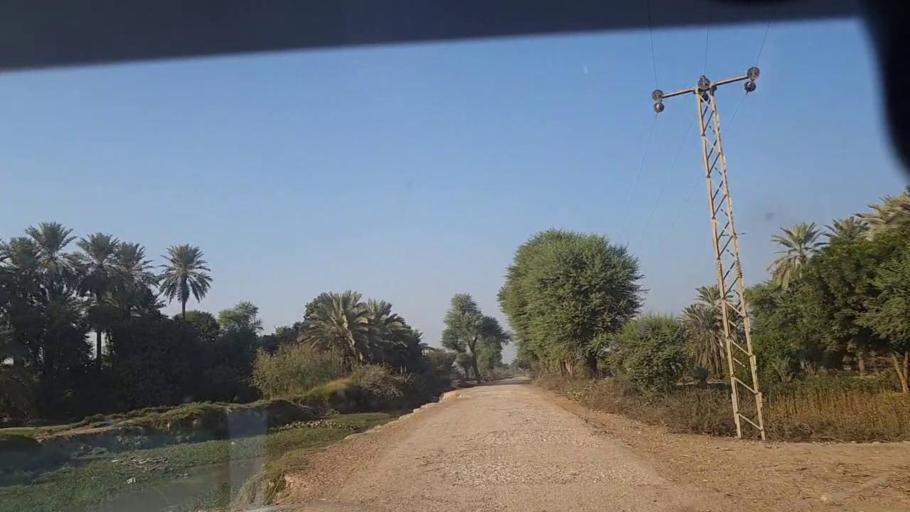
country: PK
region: Sindh
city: Sobhadero
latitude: 27.2585
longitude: 68.3510
